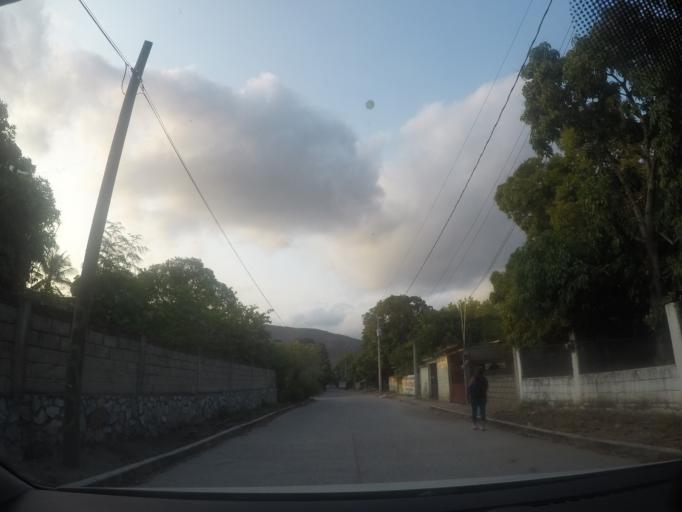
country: MX
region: Oaxaca
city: San Pedro Comitancillo
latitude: 16.5839
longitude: -95.2091
